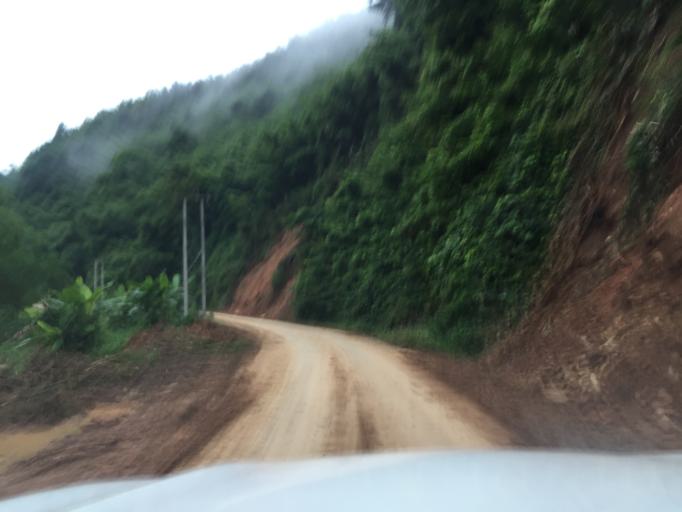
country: LA
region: Phongsali
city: Khoa
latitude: 21.0772
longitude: 102.3774
